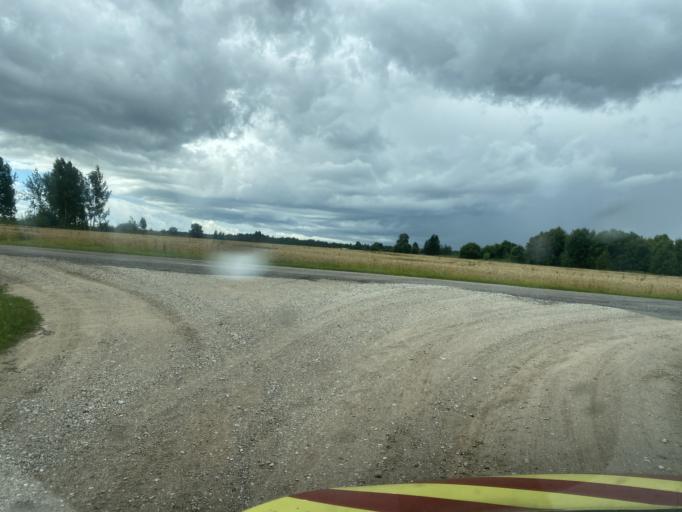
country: EE
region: Valgamaa
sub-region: Torva linn
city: Torva
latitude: 58.0916
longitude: 25.9035
